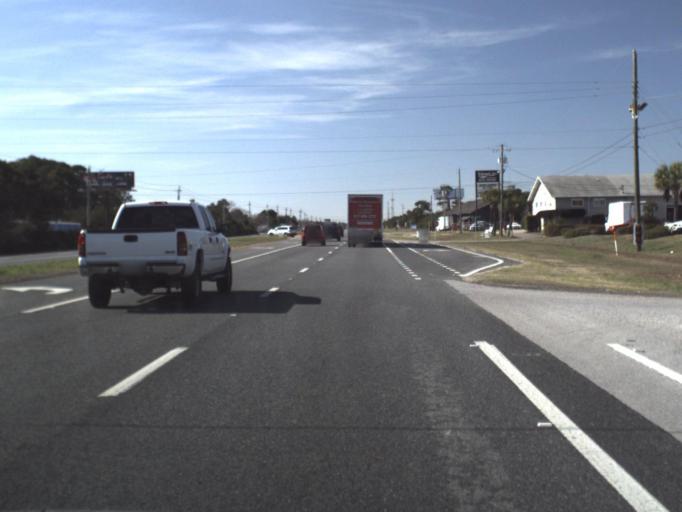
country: US
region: Florida
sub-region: Bay County
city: Laguna Beach
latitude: 30.2403
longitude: -85.9123
